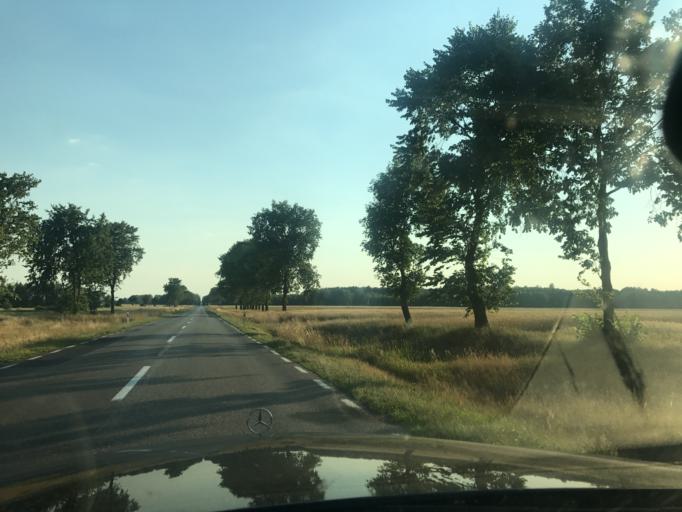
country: PL
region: Lublin Voivodeship
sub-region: Powiat parczewski
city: Jablon
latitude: 51.7324
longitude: 23.1242
